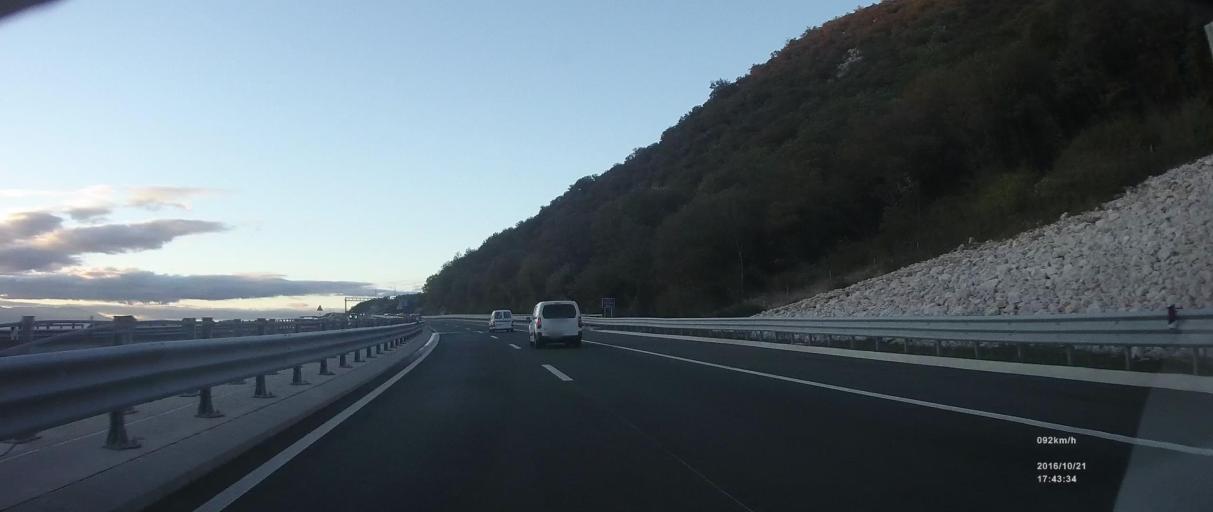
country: HR
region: Primorsko-Goranska
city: Hreljin
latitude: 45.2691
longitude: 14.6049
